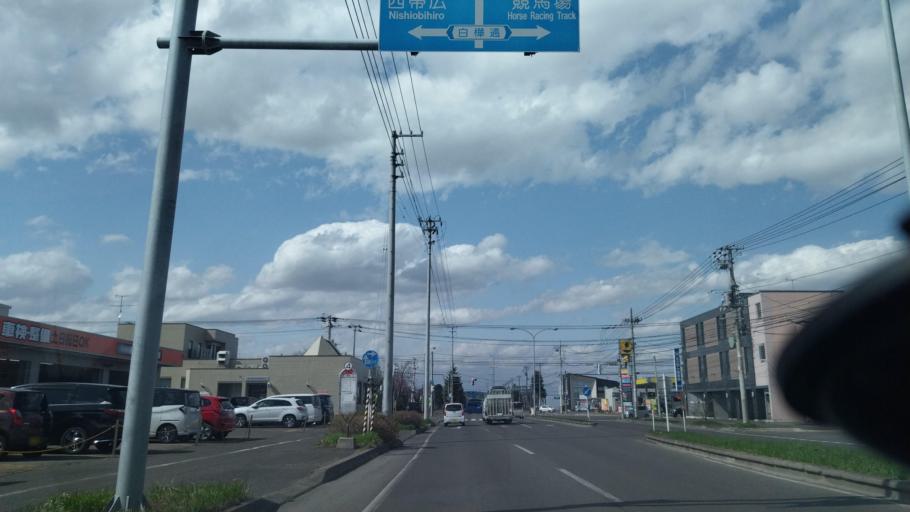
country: JP
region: Hokkaido
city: Obihiro
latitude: 42.9168
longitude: 143.1445
